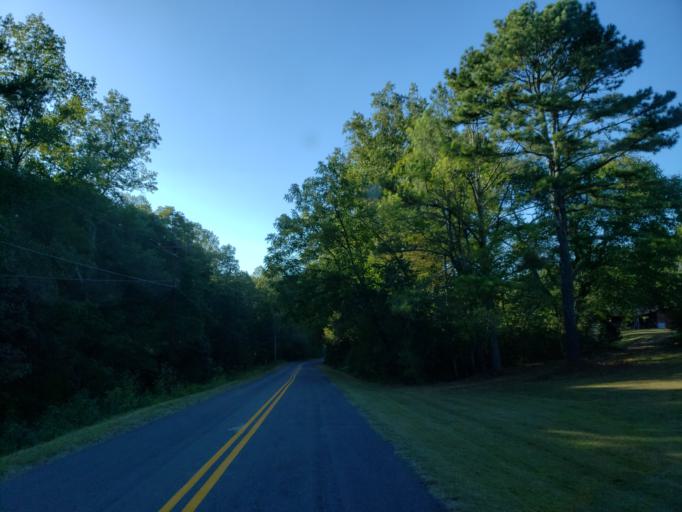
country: US
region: Georgia
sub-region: Pickens County
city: Nelson
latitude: 34.3774
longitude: -84.3947
